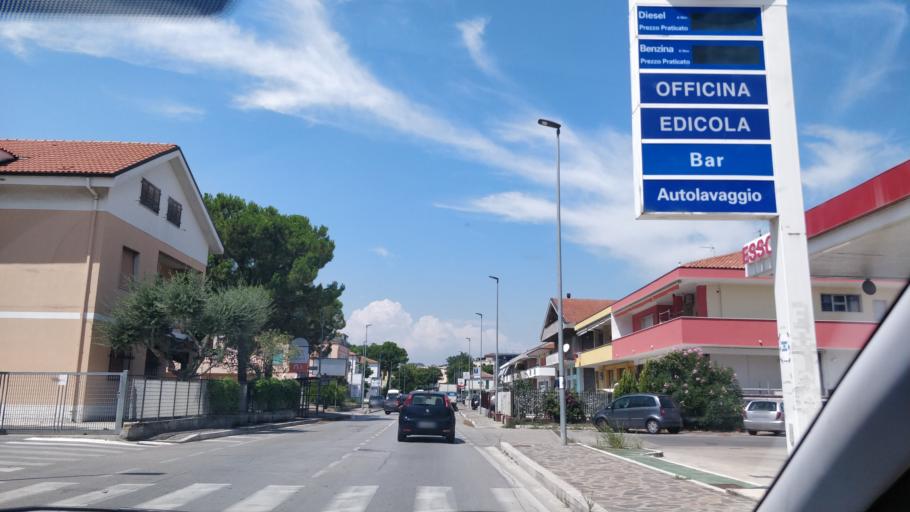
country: IT
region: Abruzzo
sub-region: Provincia di Chieti
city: Francavilla al Mare
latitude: 42.4226
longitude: 14.2827
